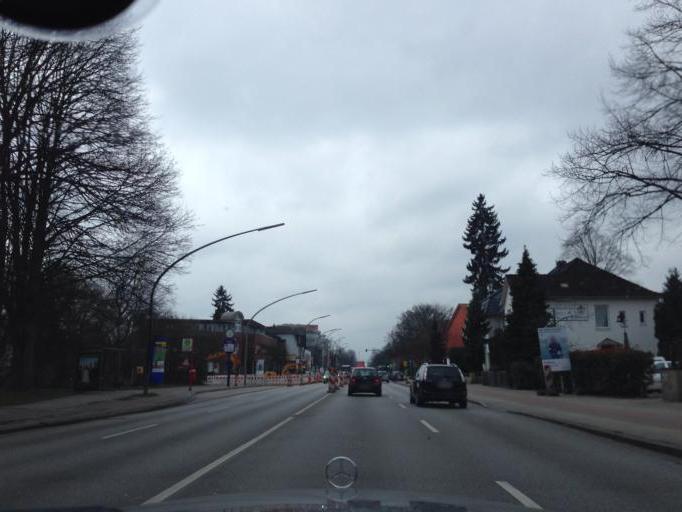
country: DE
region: Hamburg
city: Steilshoop
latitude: 53.6064
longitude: 10.0711
